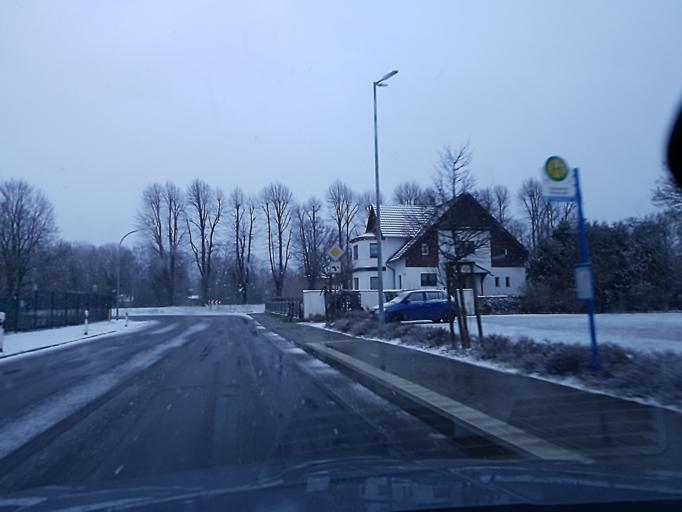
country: DE
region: Brandenburg
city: Elsterwerda
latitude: 51.4547
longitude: 13.5188
